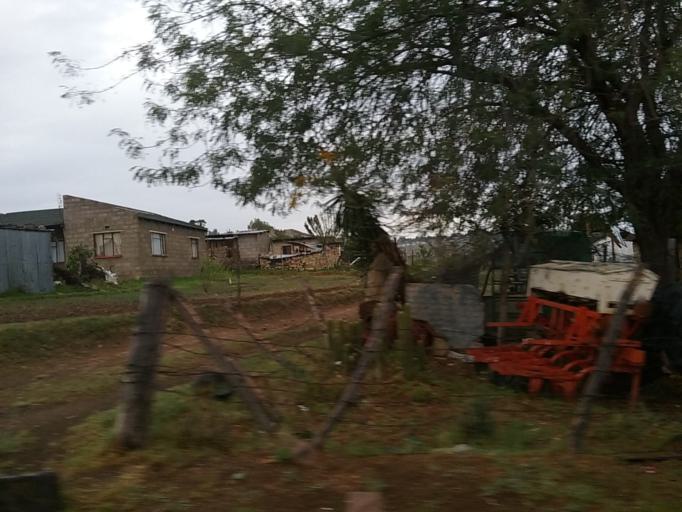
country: LS
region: Berea
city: Teyateyaneng
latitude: -29.1286
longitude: 27.7439
